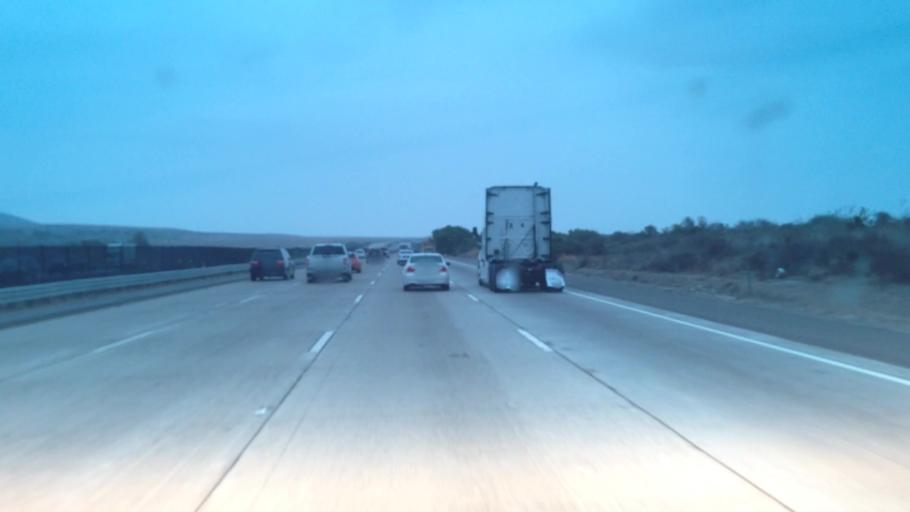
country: US
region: California
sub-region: Orange County
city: San Clemente
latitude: 33.3306
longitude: -117.4957
